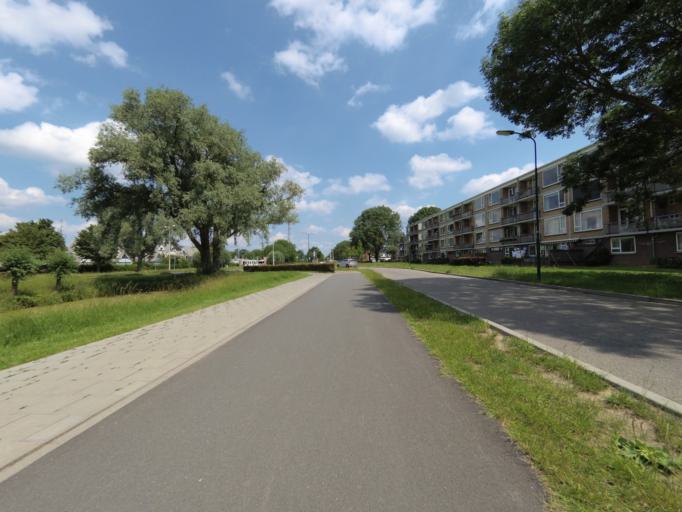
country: NL
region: Utrecht
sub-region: Gemeente Wijk bij Duurstede
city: Wijk bij Duurstede
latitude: 51.9713
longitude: 5.3359
